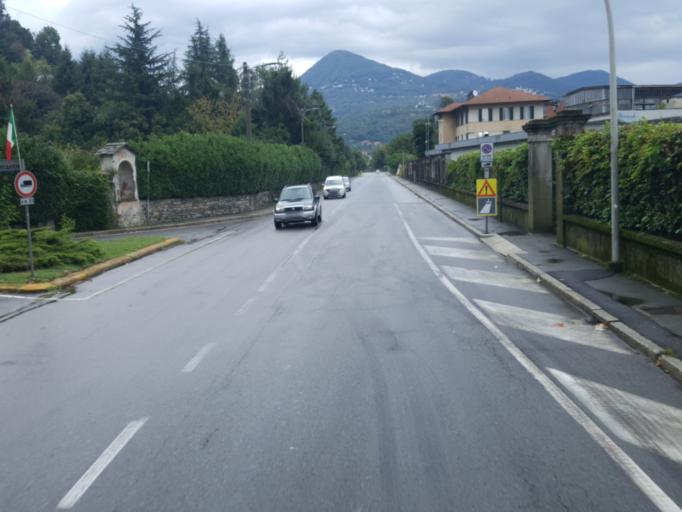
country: IT
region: Piedmont
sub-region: Provincia Verbano-Cusio-Ossola
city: Verbania
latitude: 45.9333
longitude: 8.5542
